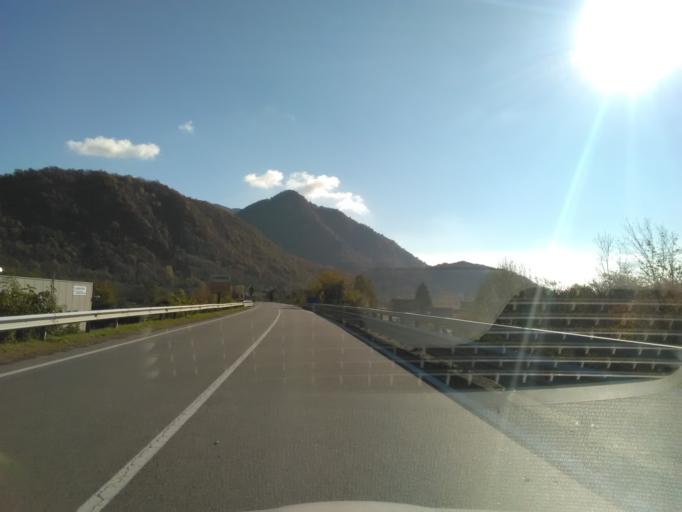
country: IT
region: Piedmont
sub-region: Provincia di Vercelli
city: Quarona
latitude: 45.7884
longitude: 8.2729
